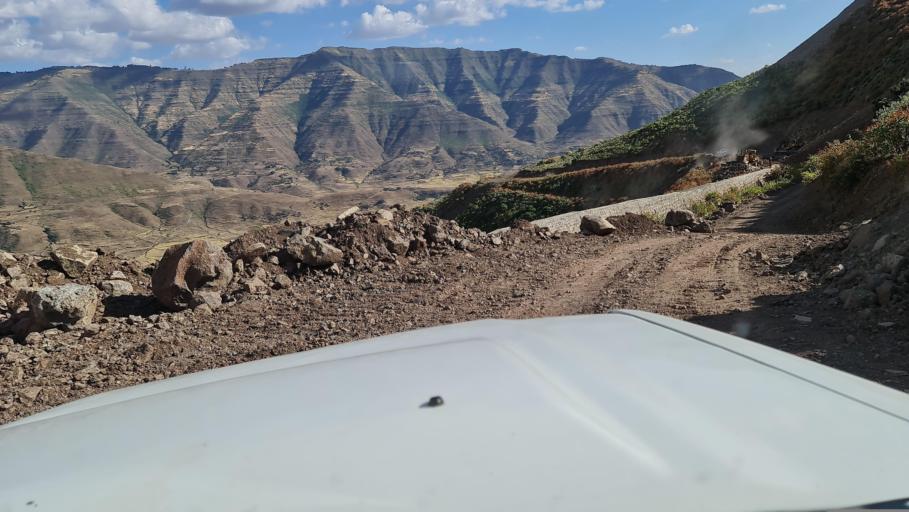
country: ET
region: Amhara
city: Debark'
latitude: 13.1266
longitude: 38.0189
